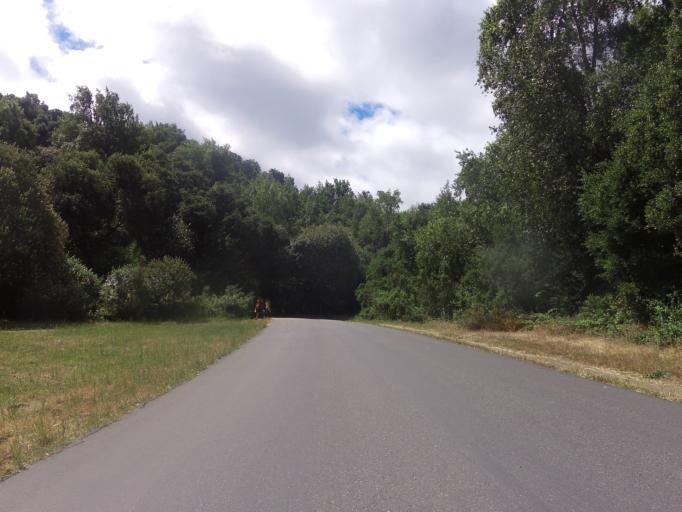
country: US
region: California
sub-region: Santa Clara County
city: Loyola
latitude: 37.3341
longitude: -122.0933
